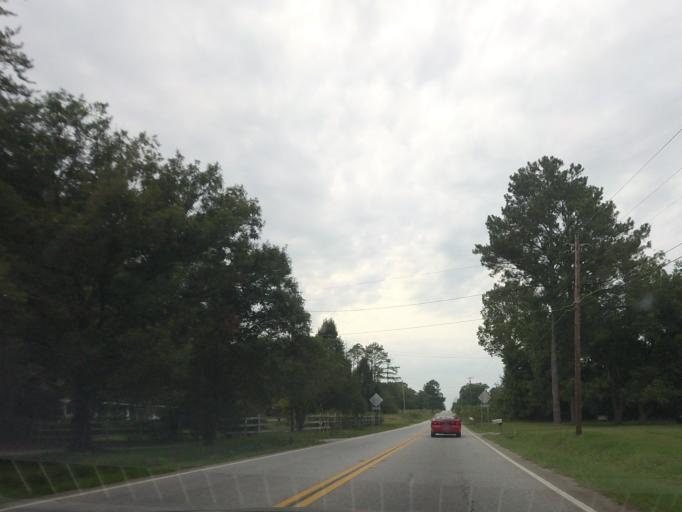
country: US
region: Georgia
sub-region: Bibb County
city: Macon
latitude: 32.8084
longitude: -83.5119
